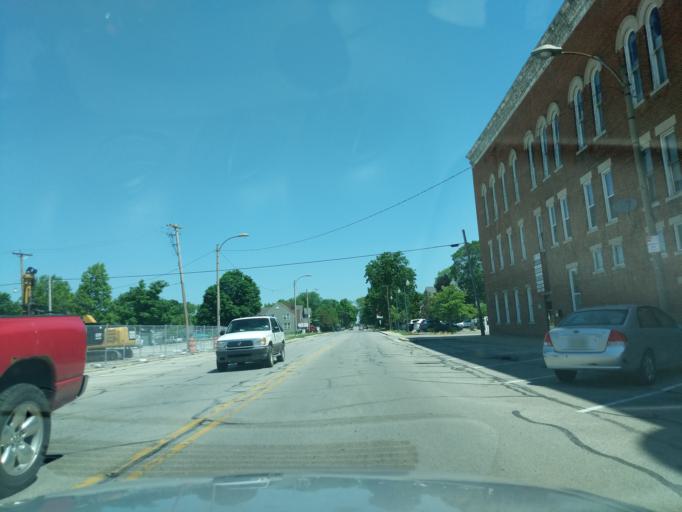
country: US
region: Indiana
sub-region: Whitley County
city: Columbia City
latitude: 41.1572
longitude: -85.4913
